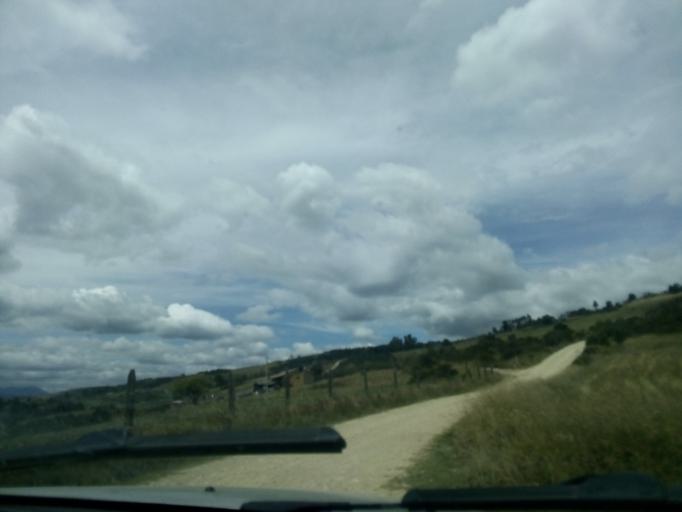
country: CO
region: Boyaca
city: Toca
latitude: 5.6231
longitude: -73.1283
